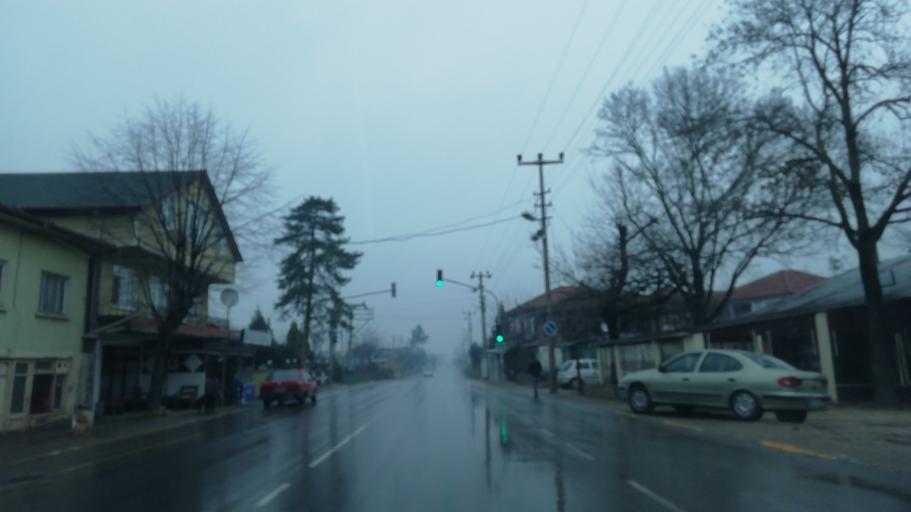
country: TR
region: Sakarya
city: Akyazi
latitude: 40.6560
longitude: 30.6172
